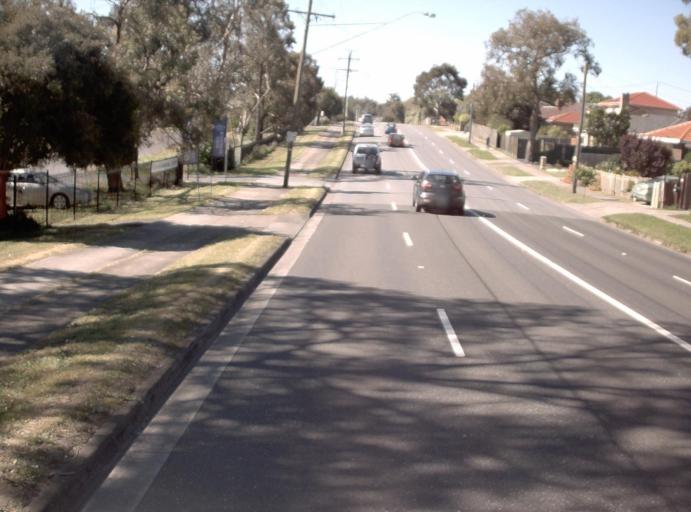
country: AU
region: Victoria
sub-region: Knox
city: Knoxfield
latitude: -37.8729
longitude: 145.2594
